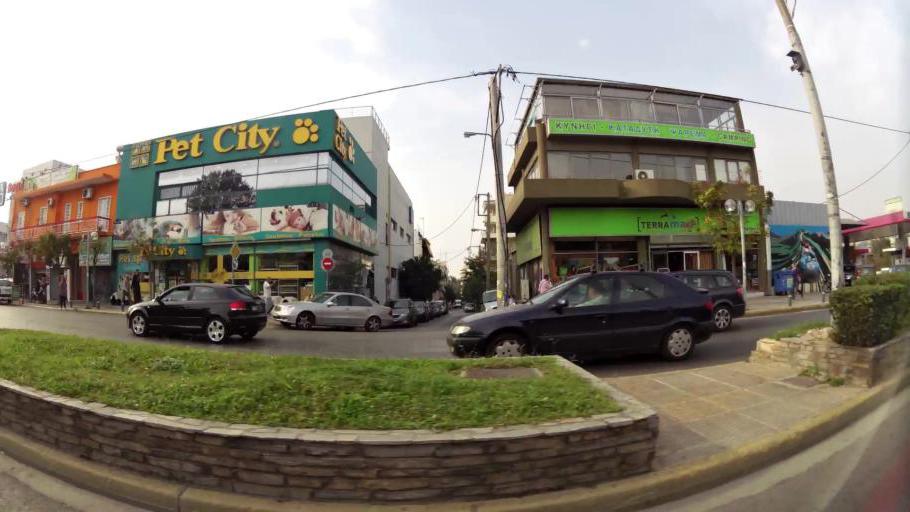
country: GR
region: Attica
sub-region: Nomarchia Athinas
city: Aigaleo
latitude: 37.9930
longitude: 23.6768
